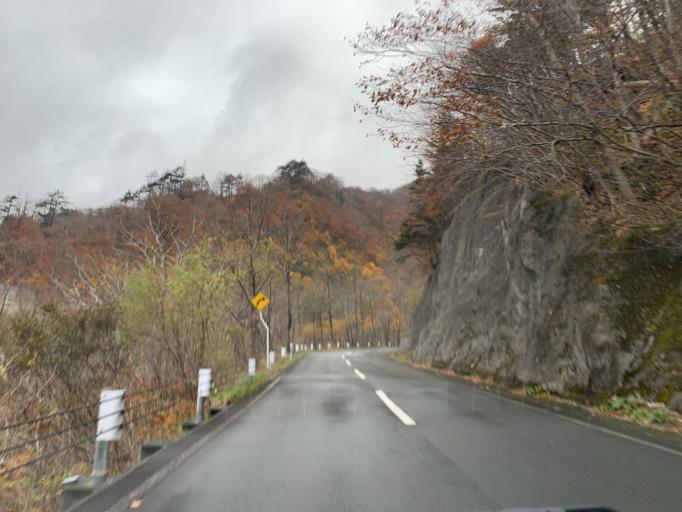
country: JP
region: Iwate
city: Mizusawa
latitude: 39.1243
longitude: 140.8285
